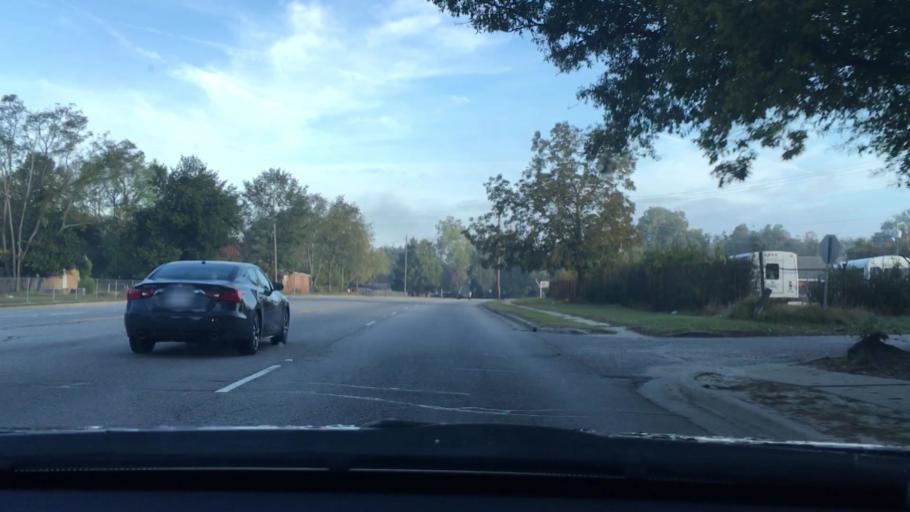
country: US
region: South Carolina
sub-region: Sumter County
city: South Sumter
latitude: 33.9011
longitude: -80.3371
